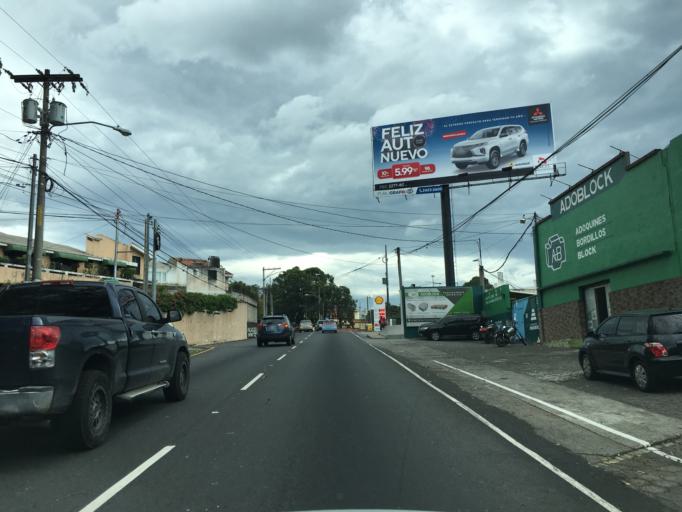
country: GT
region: Guatemala
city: Mixco
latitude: 14.5944
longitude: -90.5669
